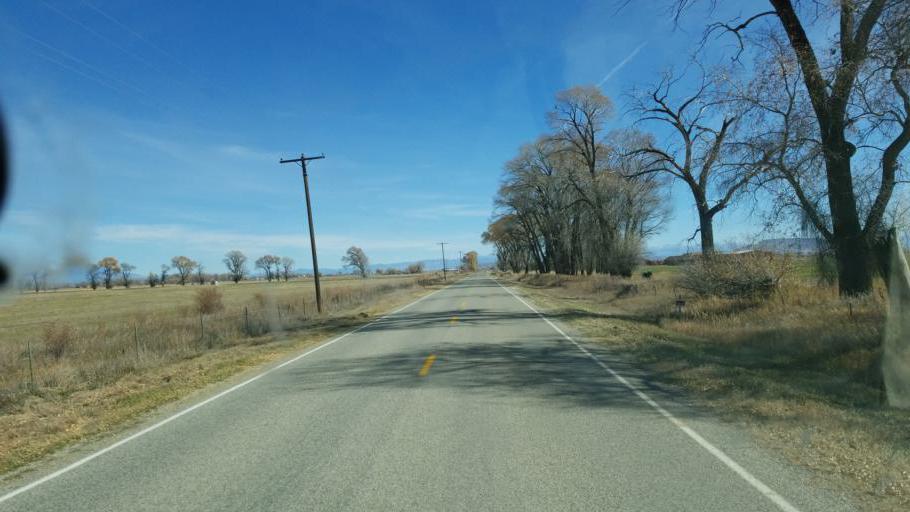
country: US
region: Colorado
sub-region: Conejos County
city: Conejos
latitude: 37.2836
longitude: -106.0428
